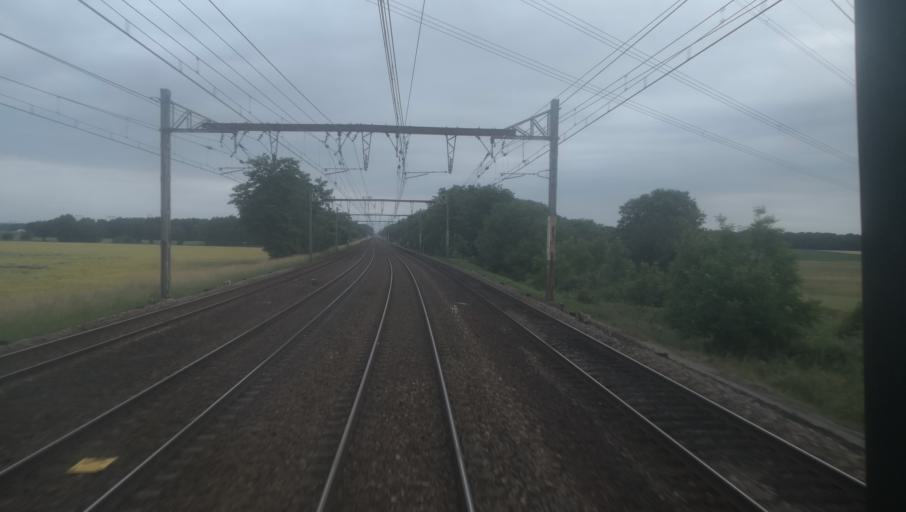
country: FR
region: Ile-de-France
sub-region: Departement de l'Essonne
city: Cheptainville
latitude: 48.5395
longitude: 2.2934
